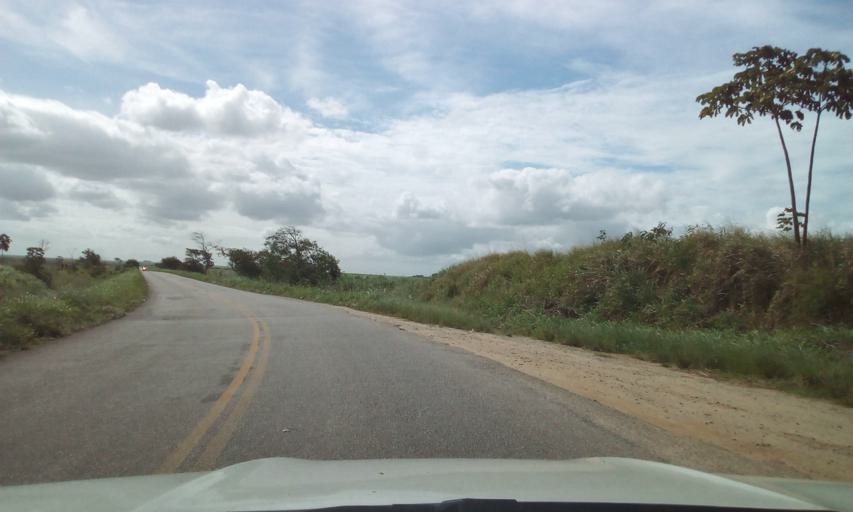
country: BR
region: Paraiba
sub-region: Santa Rita
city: Santa Rita
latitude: -7.0799
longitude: -34.9843
